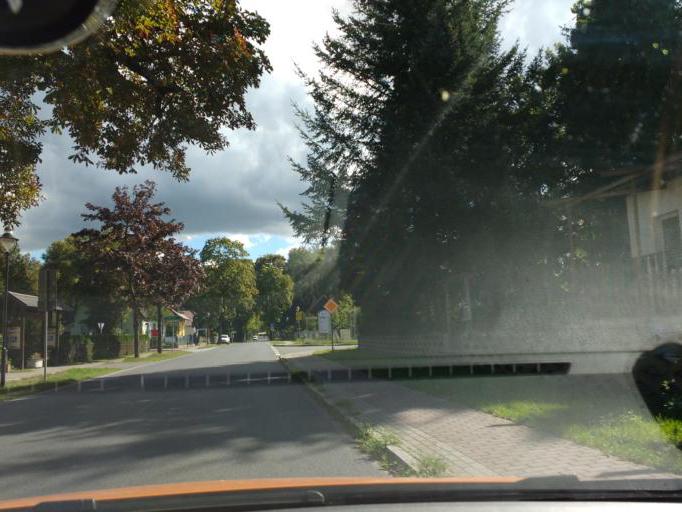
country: DE
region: Brandenburg
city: Munchehofe
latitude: 52.2254
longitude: 13.7680
